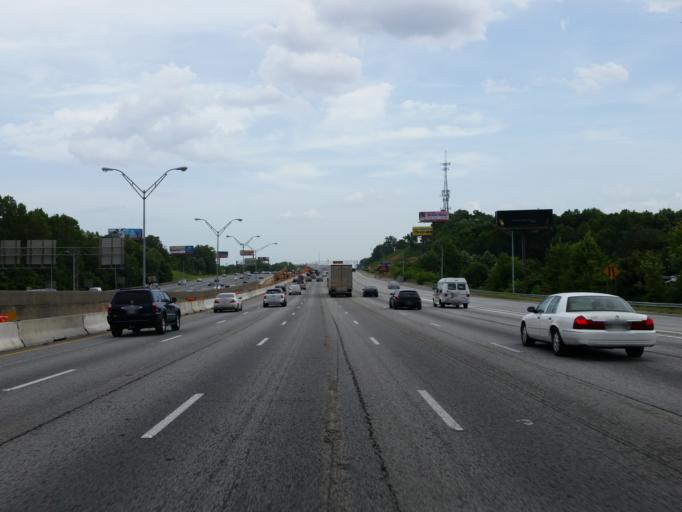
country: US
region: Georgia
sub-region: Cobb County
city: Smyrna
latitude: 33.9206
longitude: -84.4843
